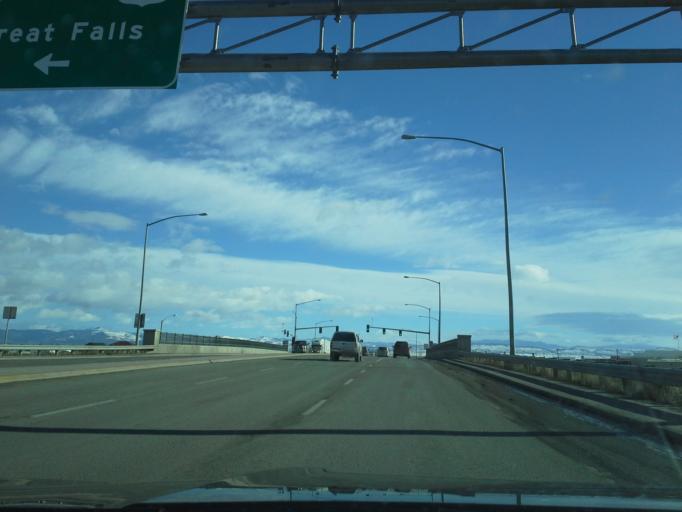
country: US
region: Montana
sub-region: Lewis and Clark County
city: Helena
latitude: 46.6165
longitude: -112.0123
